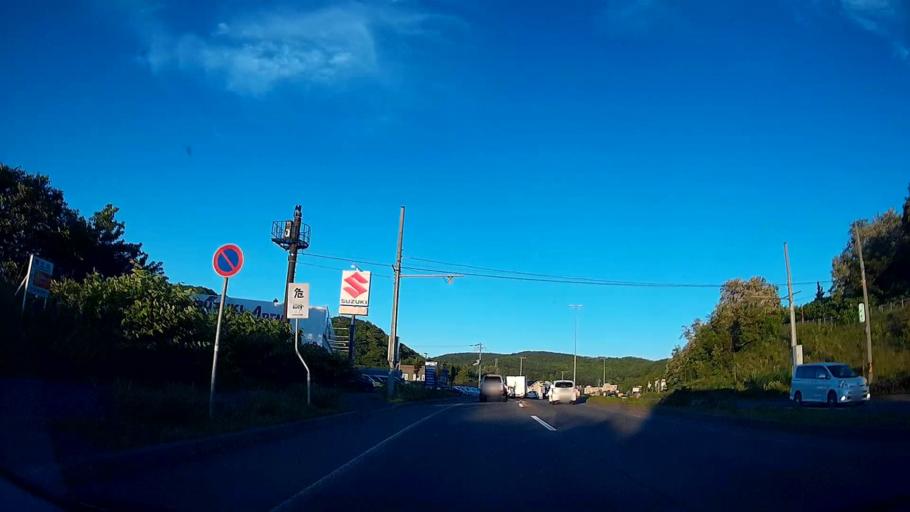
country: JP
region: Hokkaido
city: Otaru
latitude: 43.2109
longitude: 140.9176
